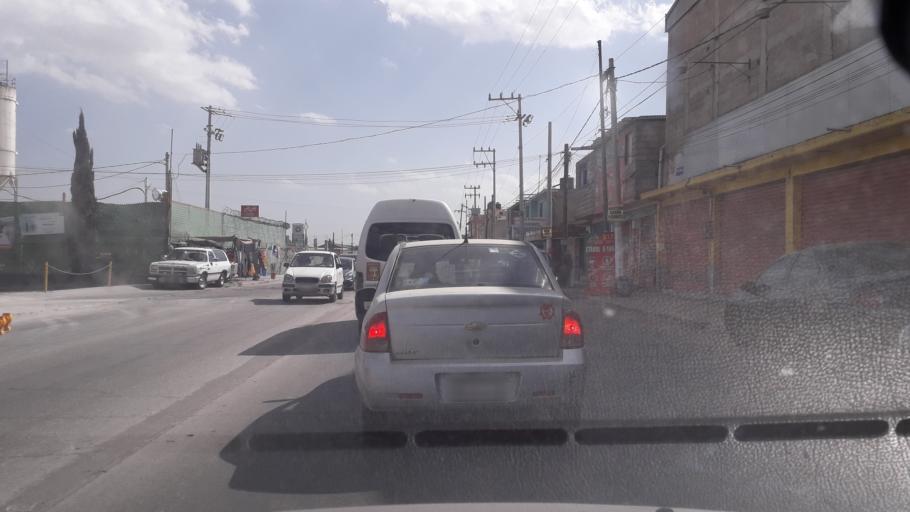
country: MX
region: Mexico
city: Ecatepec
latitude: 19.6220
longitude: -99.0469
